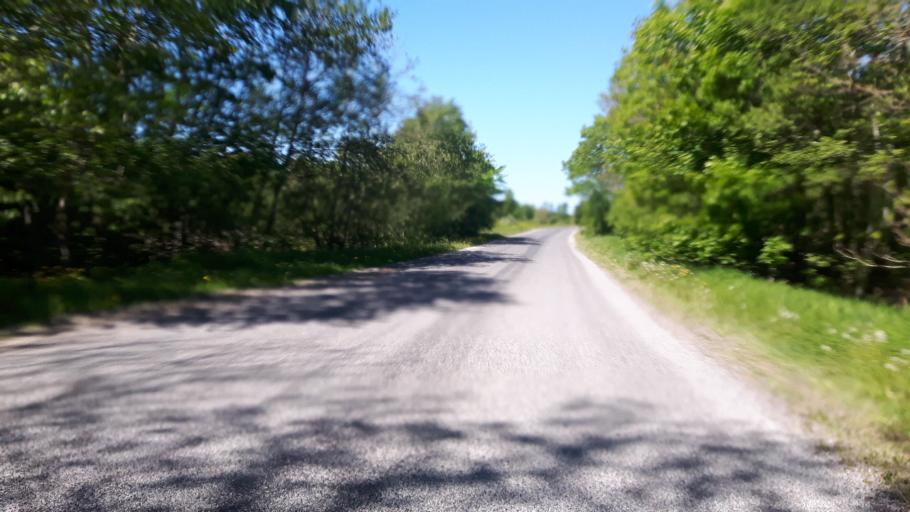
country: EE
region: Ida-Virumaa
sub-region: Sillamaee linn
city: Sillamae
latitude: 59.3777
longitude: 27.8346
